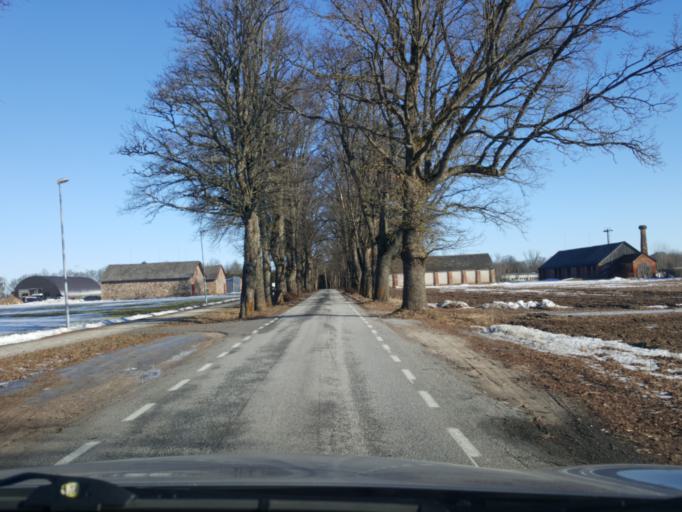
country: EE
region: Viljandimaa
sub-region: Vohma linn
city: Vohma
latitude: 58.5504
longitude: 25.5569
